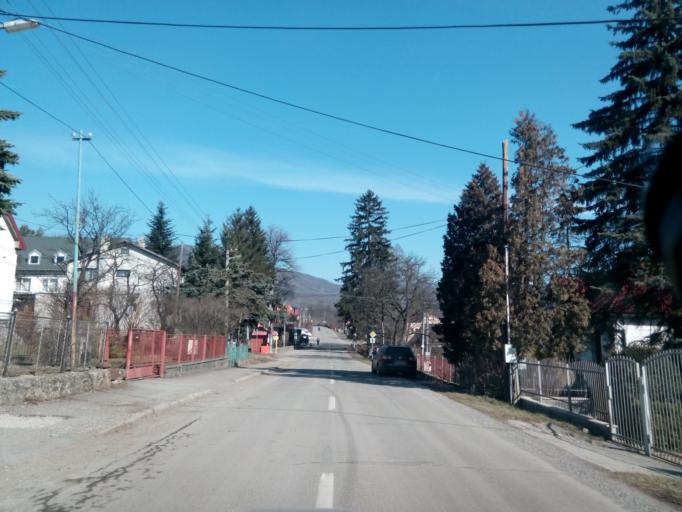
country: SK
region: Kosicky
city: Sobrance
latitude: 48.8477
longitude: 22.1838
